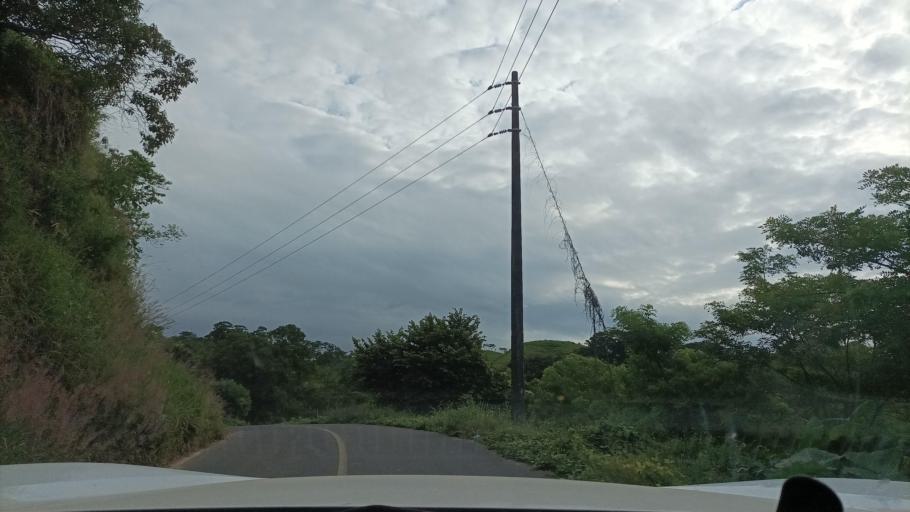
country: MX
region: Veracruz
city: Hidalgotitlan
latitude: 17.6879
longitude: -94.4641
